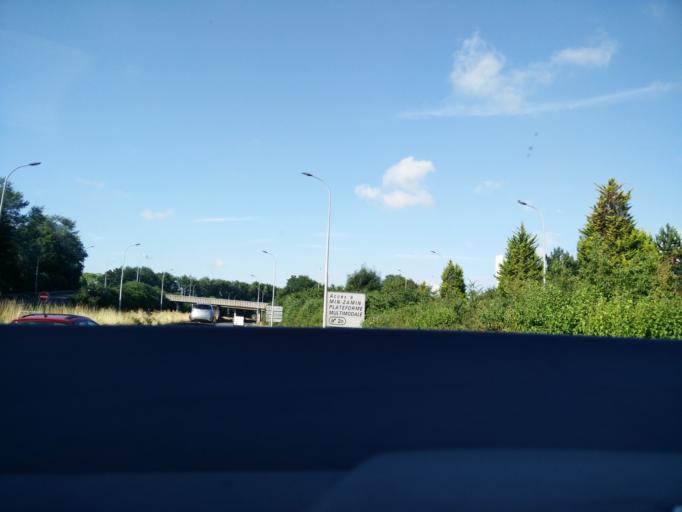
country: FR
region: Nord-Pas-de-Calais
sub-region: Departement du Nord
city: Lomme
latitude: 50.6509
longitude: 2.9860
